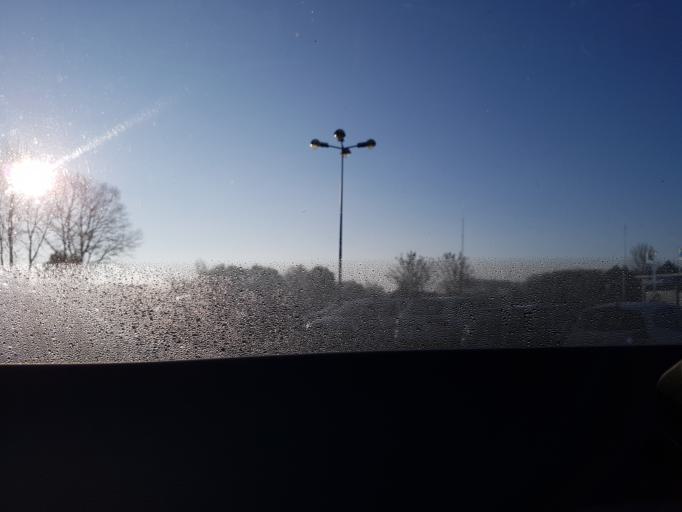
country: FR
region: Nord-Pas-de-Calais
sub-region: Departement du Nord
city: Watten
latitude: 50.8219
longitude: 2.1998
